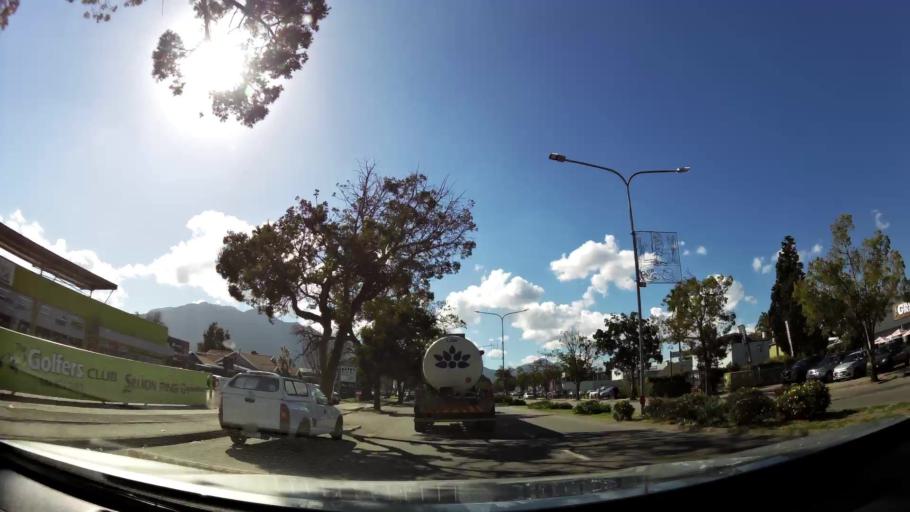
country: ZA
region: Western Cape
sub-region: Eden District Municipality
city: George
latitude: -33.9663
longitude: 22.4508
